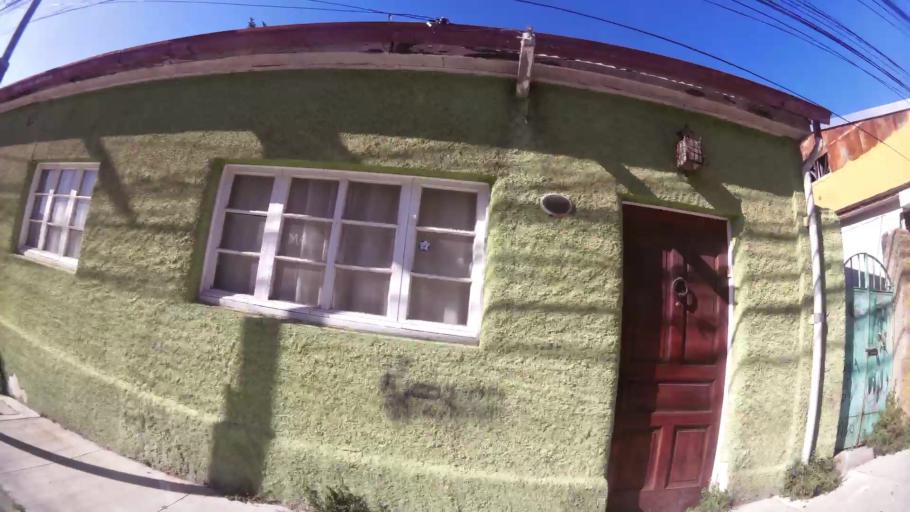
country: CL
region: Valparaiso
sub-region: Provincia de Valparaiso
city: Valparaiso
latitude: -33.0444
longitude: -71.6306
